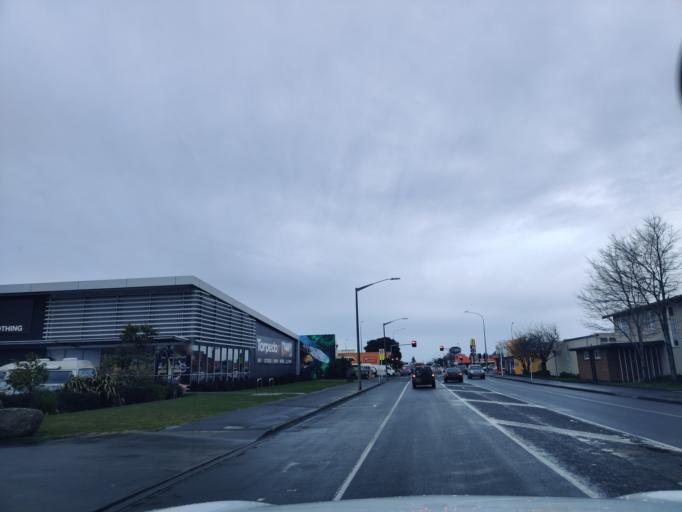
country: NZ
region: Manawatu-Wanganui
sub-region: Palmerston North City
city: Palmerston North
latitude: -40.3493
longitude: 175.6076
